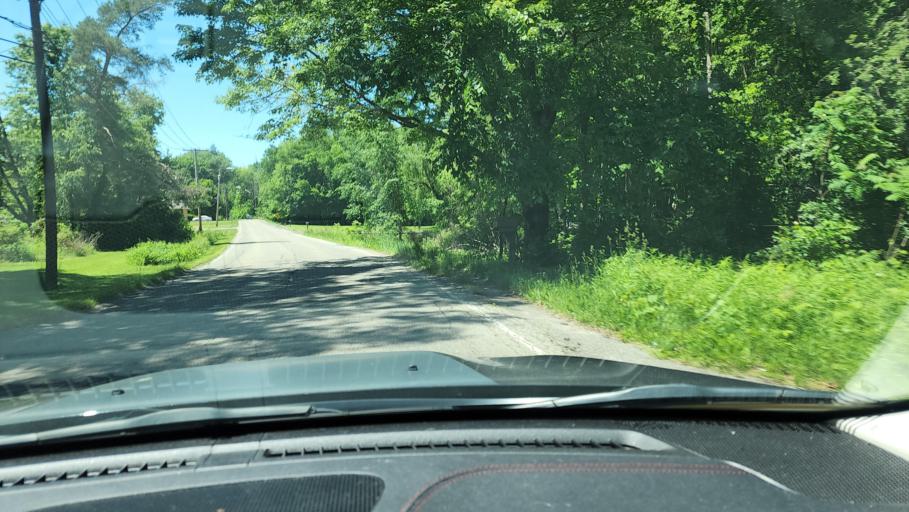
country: US
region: Ohio
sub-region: Trumbull County
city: Niles
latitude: 41.1670
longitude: -80.7803
